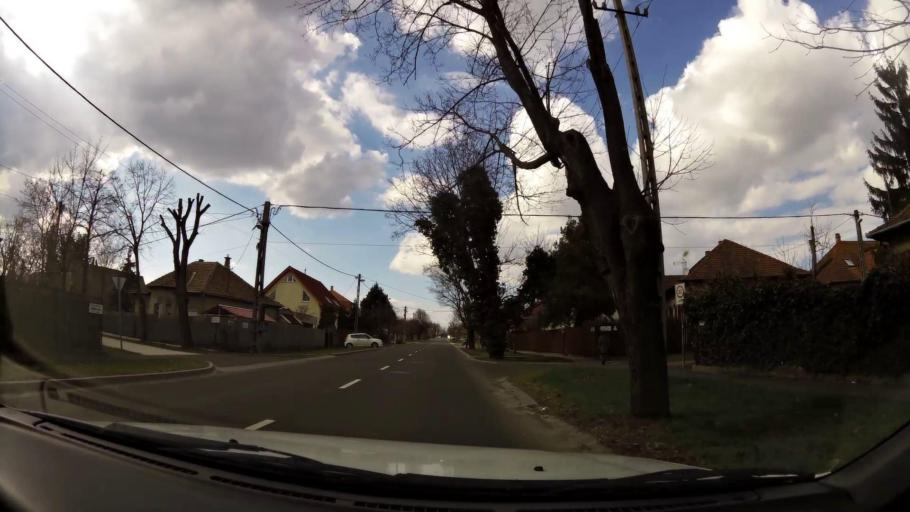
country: HU
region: Budapest
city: Budapest XVII. keruelet
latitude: 47.4922
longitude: 19.2810
